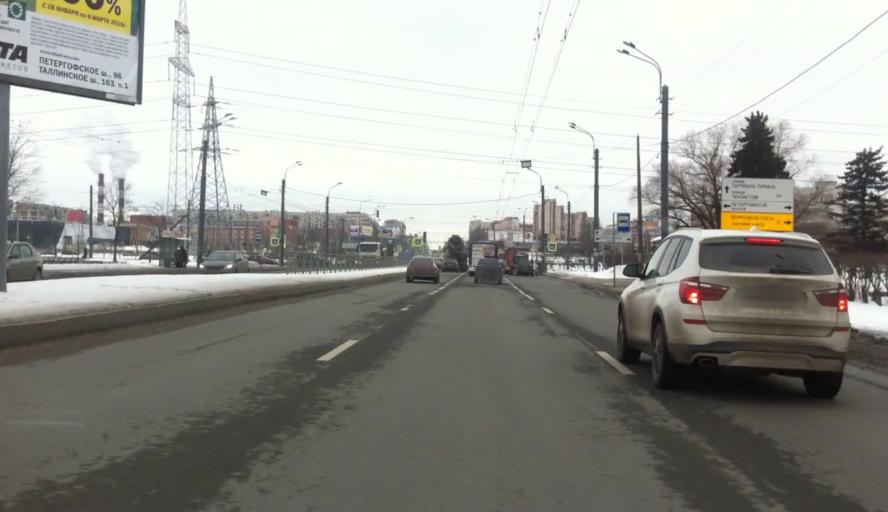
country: RU
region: St.-Petersburg
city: Uritsk
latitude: 59.8484
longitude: 30.1754
